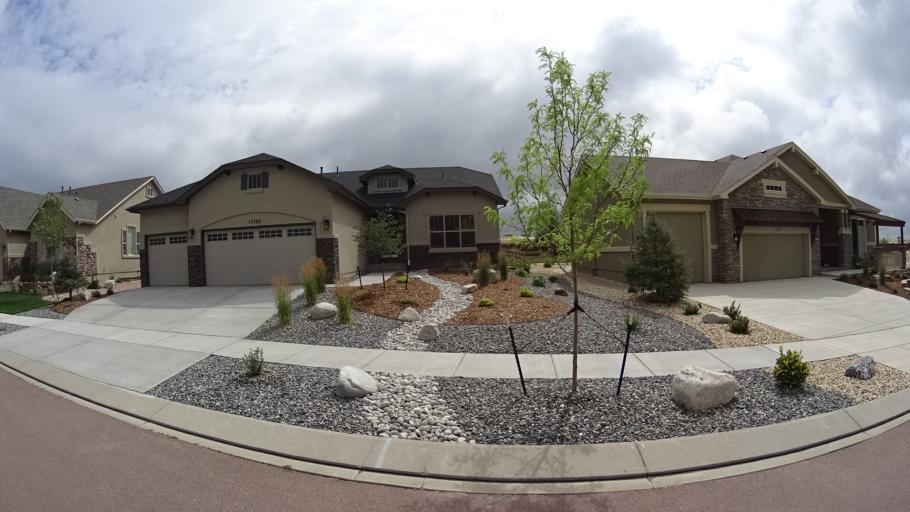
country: US
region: Colorado
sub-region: El Paso County
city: Gleneagle
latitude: 39.0133
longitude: -104.7867
